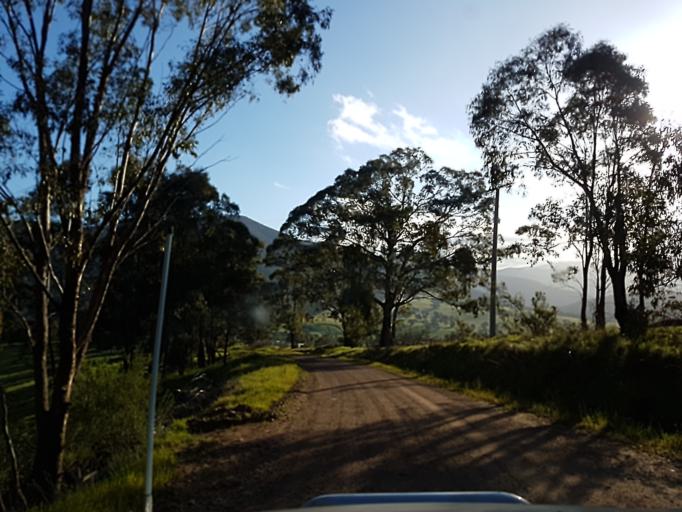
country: AU
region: Victoria
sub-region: East Gippsland
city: Bairnsdale
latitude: -37.4890
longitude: 147.1908
